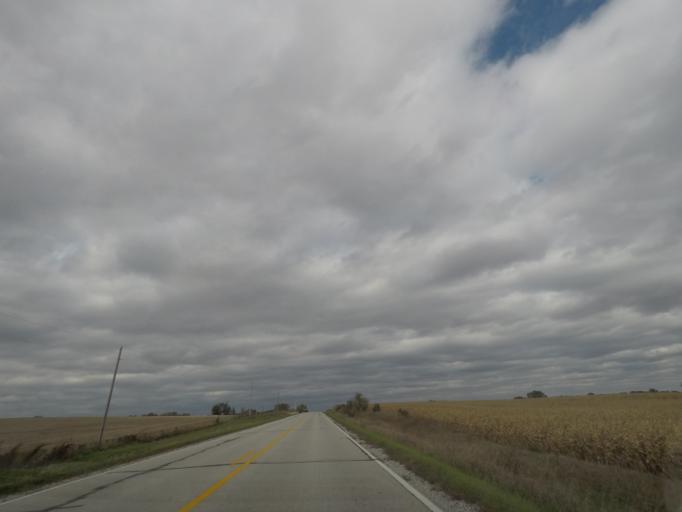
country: US
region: Iowa
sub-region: Story County
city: Huxley
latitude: 41.8571
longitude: -93.5316
